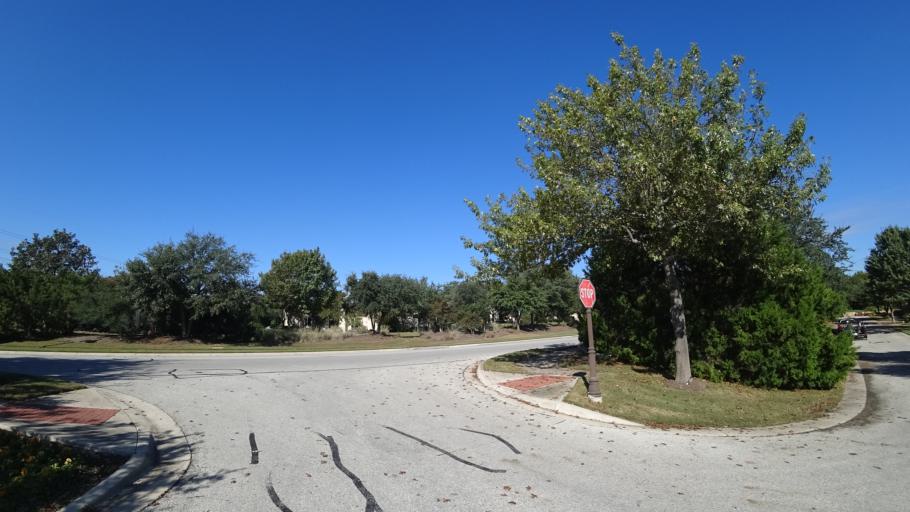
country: US
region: Texas
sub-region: Travis County
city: Hudson Bend
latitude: 30.3608
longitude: -97.8875
